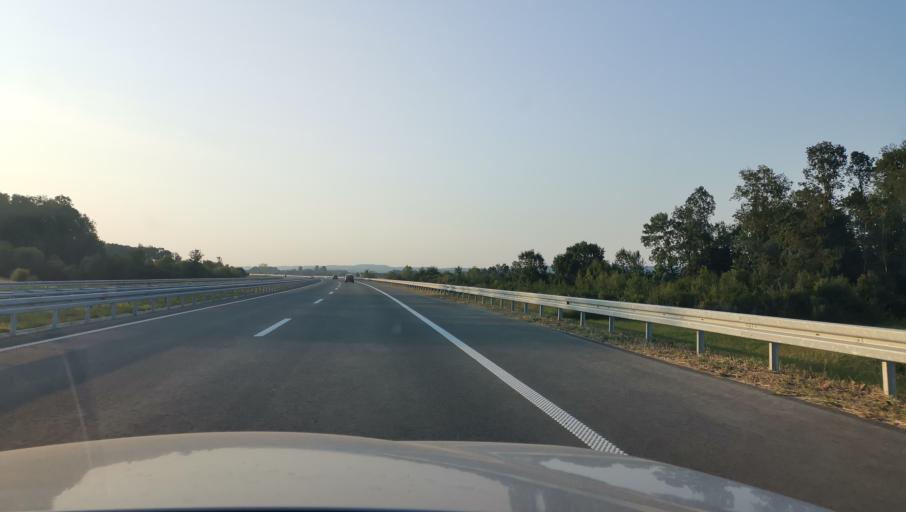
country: RS
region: Central Serbia
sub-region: Kolubarski Okrug
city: Ljig
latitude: 44.2720
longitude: 20.2677
